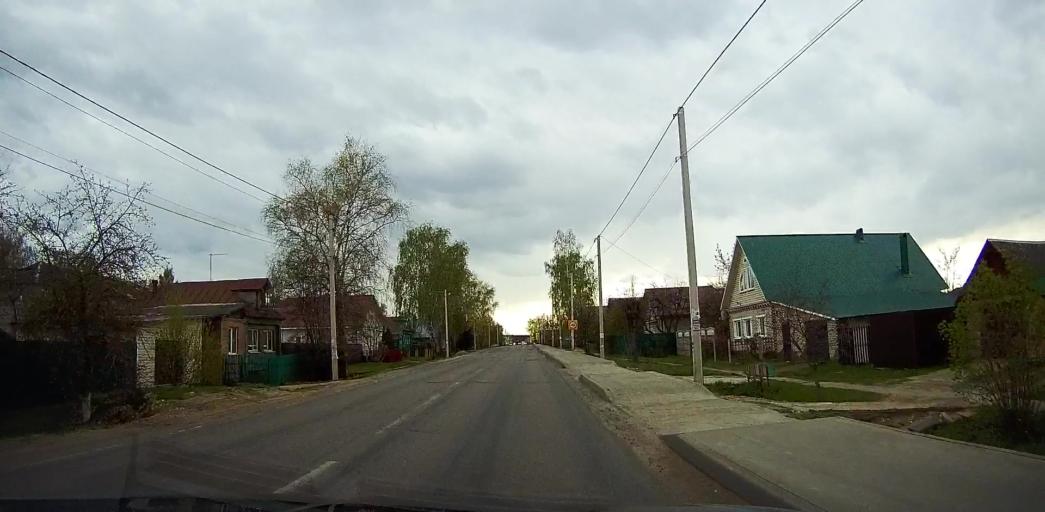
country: RU
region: Moskovskaya
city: Pavlovskiy Posad
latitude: 55.7570
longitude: 38.7078
